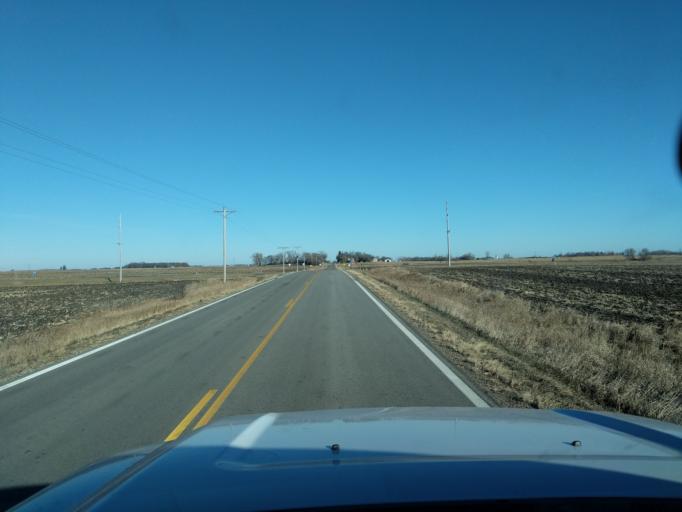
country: US
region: Minnesota
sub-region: Yellow Medicine County
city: Granite Falls
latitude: 44.7875
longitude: -95.4017
